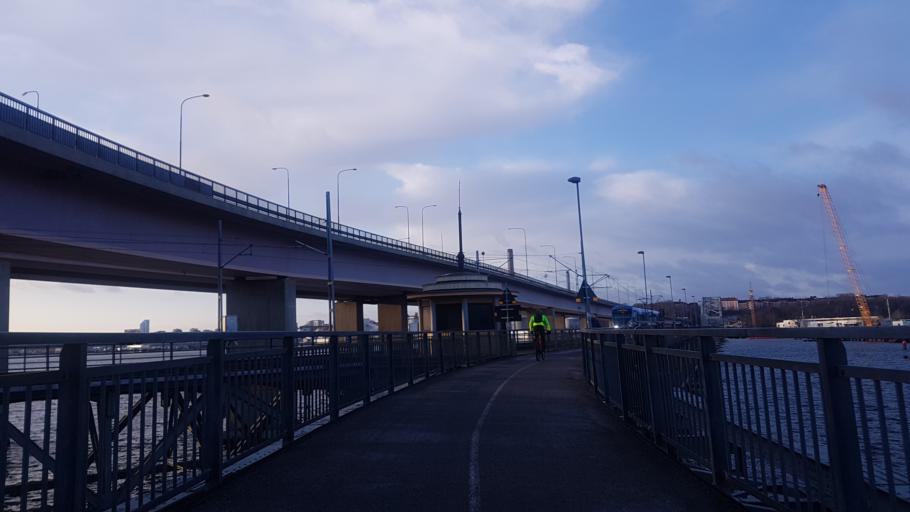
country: SE
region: Stockholm
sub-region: Lidingo
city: Lidingoe
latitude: 59.3631
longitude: 18.1145
